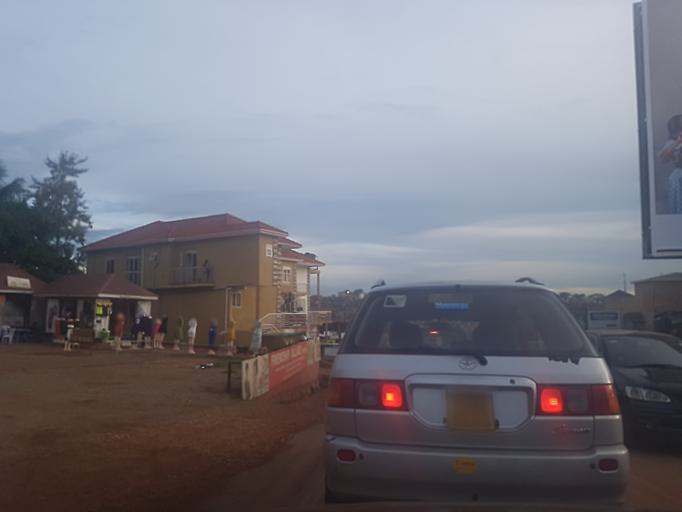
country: UG
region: Central Region
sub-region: Wakiso District
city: Kireka
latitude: 0.3762
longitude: 32.6442
